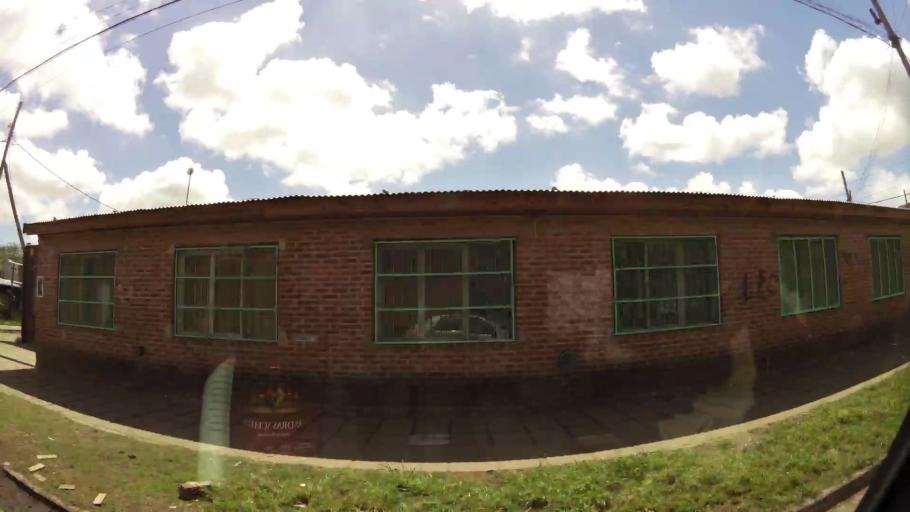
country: AR
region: Buenos Aires
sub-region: Partido de Quilmes
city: Quilmes
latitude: -34.8355
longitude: -58.2361
